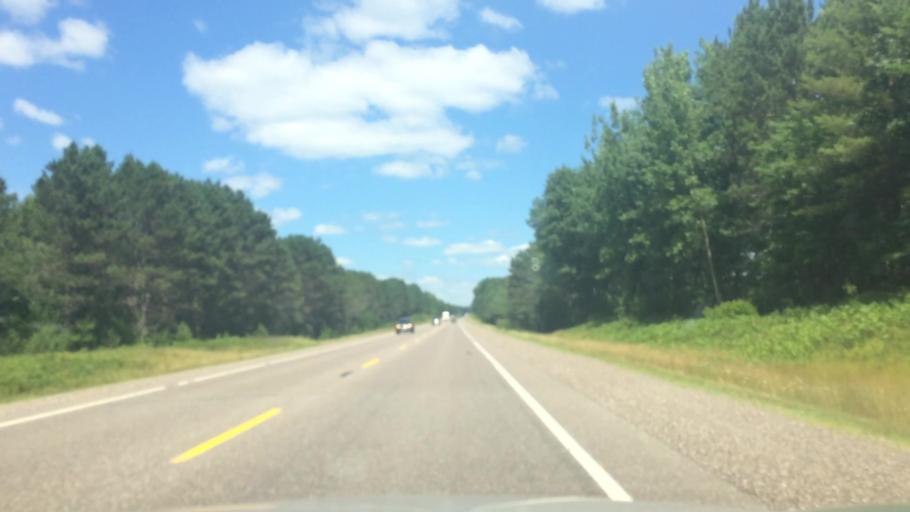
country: US
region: Wisconsin
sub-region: Vilas County
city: Lac du Flambeau
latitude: 45.9639
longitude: -89.7001
